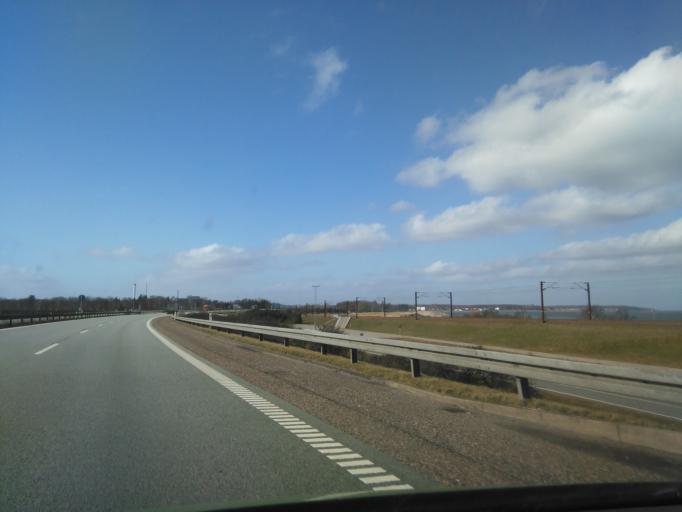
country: DK
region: South Denmark
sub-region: Nyborg Kommune
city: Nyborg
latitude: 55.2987
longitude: 10.8387
